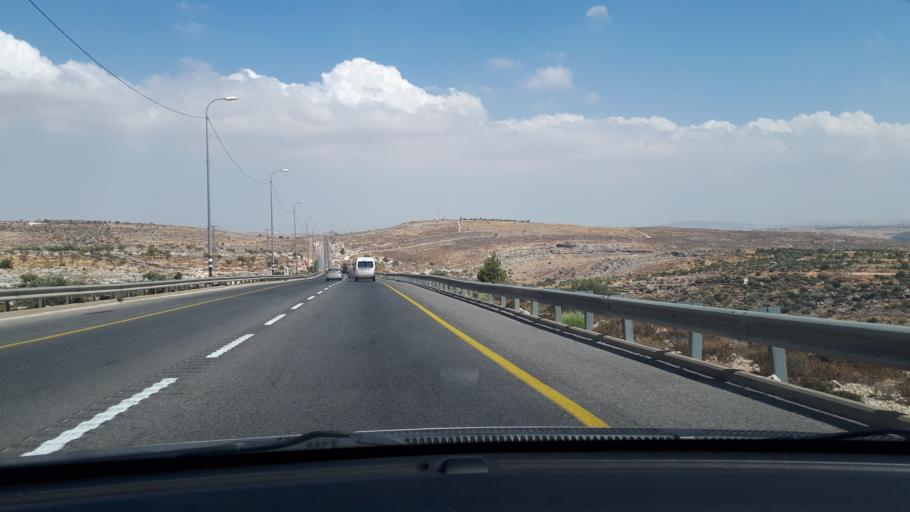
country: PS
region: West Bank
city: Burqah
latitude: 31.9023
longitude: 35.2596
